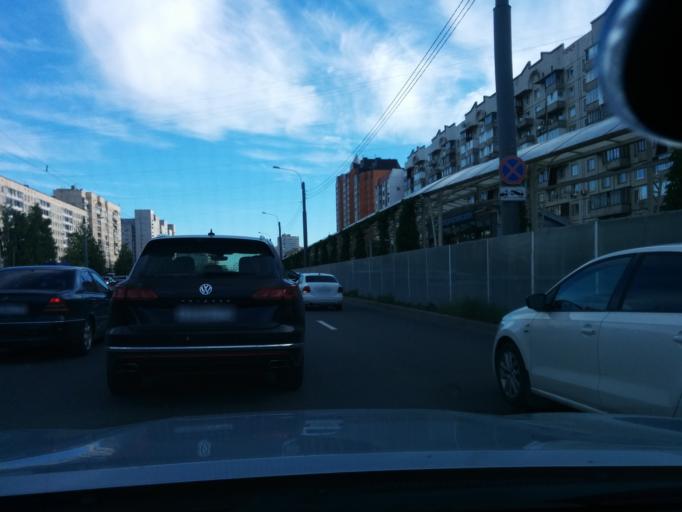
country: RU
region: Leningrad
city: Parnas
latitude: 60.0561
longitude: 30.3371
